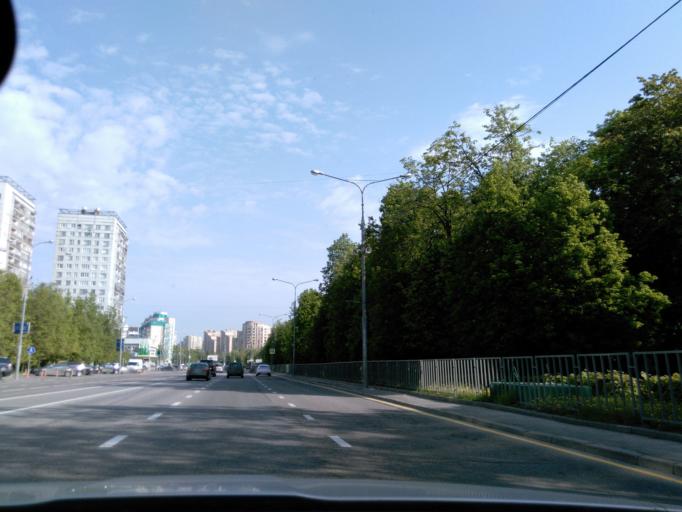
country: RU
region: Moscow
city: Zelenograd
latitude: 55.9986
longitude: 37.2109
